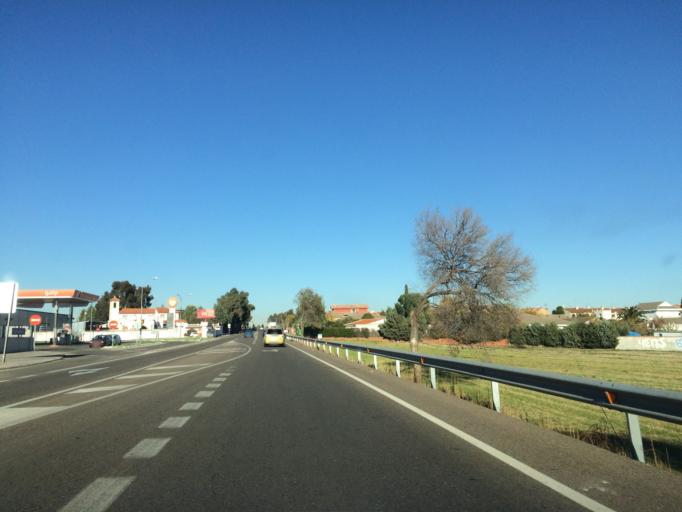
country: ES
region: Castille-La Mancha
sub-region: Province of Toledo
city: Carranque
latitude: 40.1813
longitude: -3.8868
